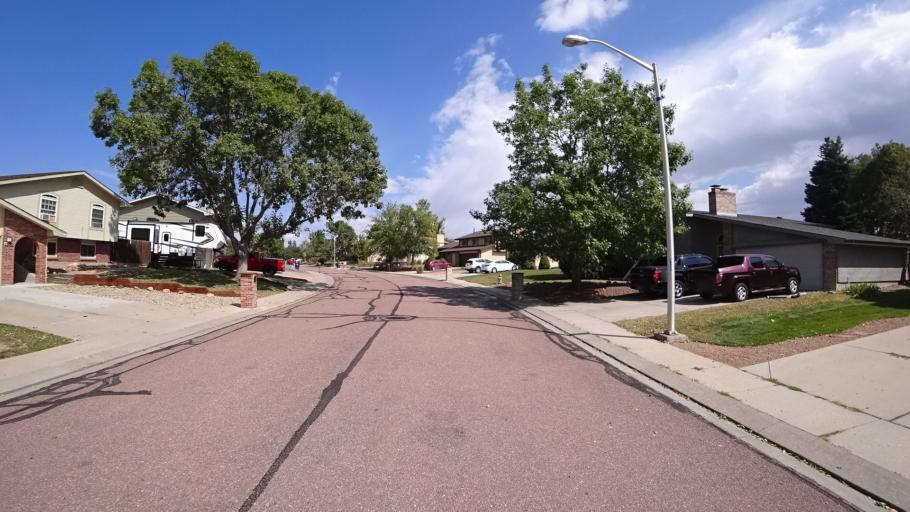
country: US
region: Colorado
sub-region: El Paso County
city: Cimarron Hills
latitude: 38.8607
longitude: -104.7262
